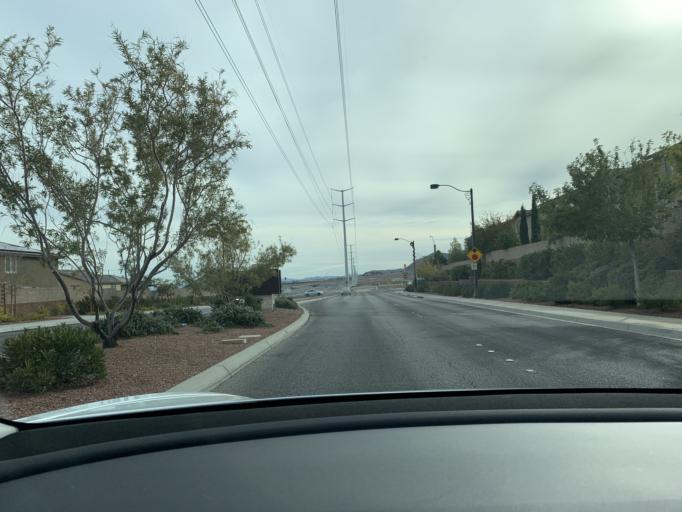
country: US
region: Nevada
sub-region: Clark County
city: Summerlin South
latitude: 36.2783
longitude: -115.3289
